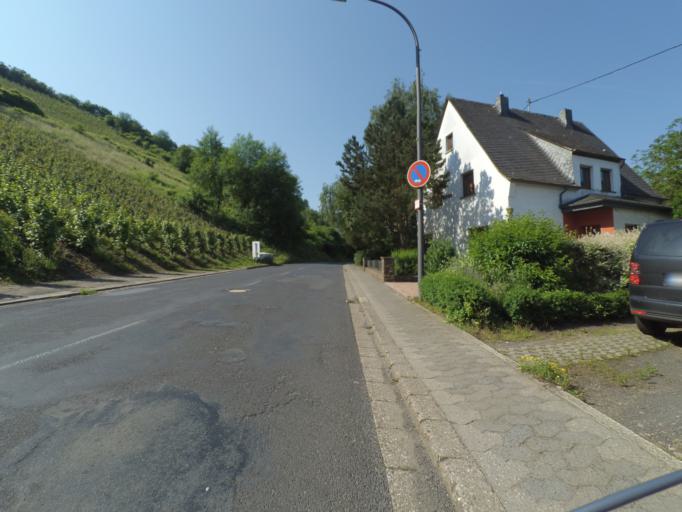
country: DE
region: Rheinland-Pfalz
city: Treis-Karden
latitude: 50.1702
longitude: 7.2997
